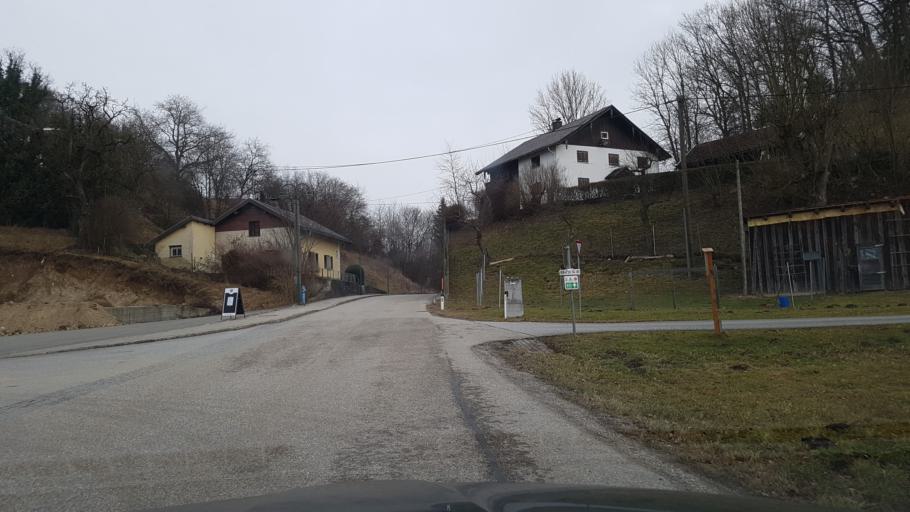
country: AT
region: Salzburg
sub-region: Politischer Bezirk Salzburg-Umgebung
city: Dorfbeuern
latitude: 48.0642
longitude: 12.9621
